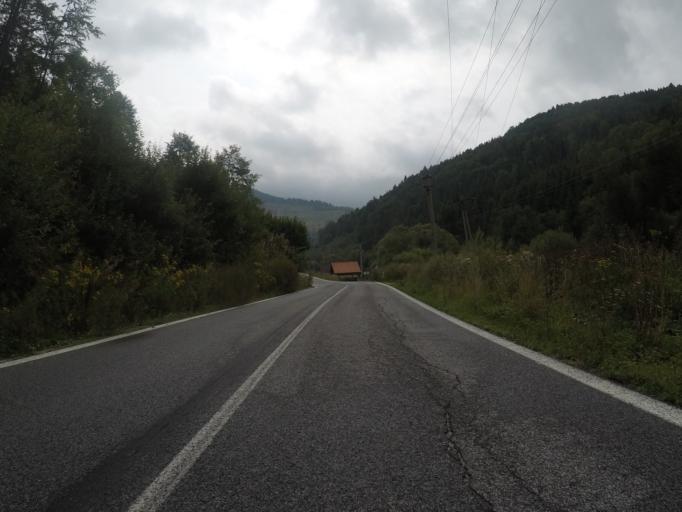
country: SK
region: Kosicky
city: Dobsina
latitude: 48.8450
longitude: 20.4281
